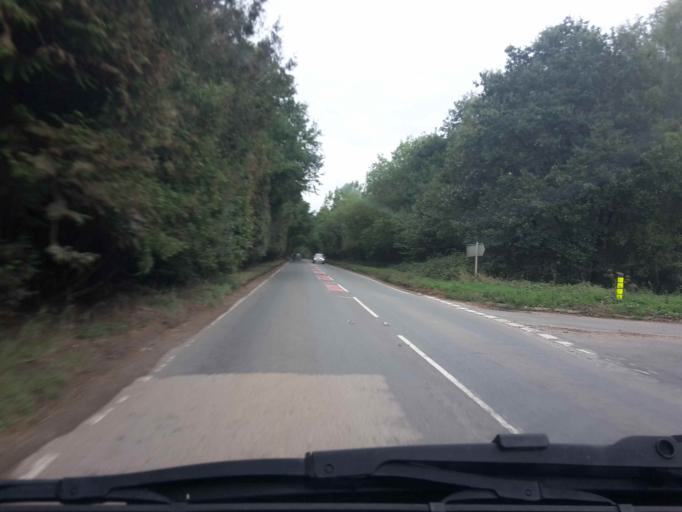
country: GB
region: England
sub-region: Hampshire
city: Eversley
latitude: 51.3262
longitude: -0.8716
